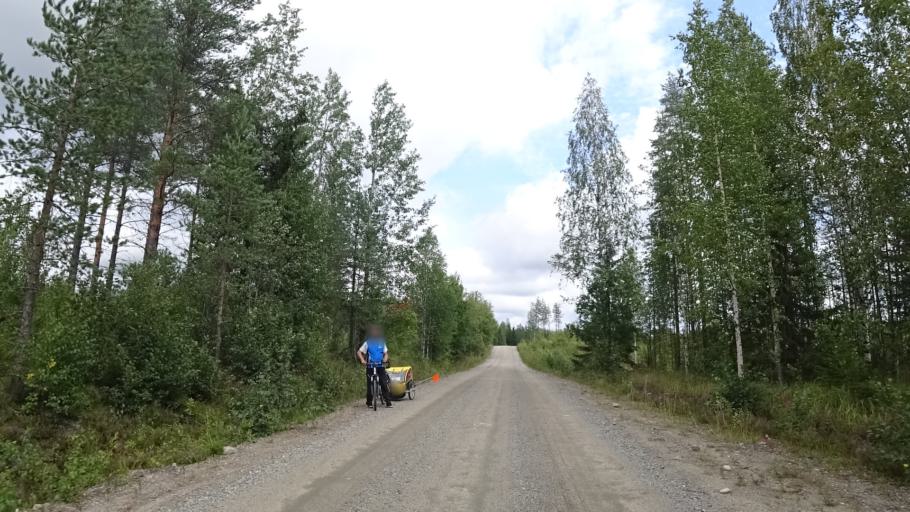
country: FI
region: North Karelia
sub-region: Joensuu
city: Ilomantsi
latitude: 62.9248
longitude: 31.3590
